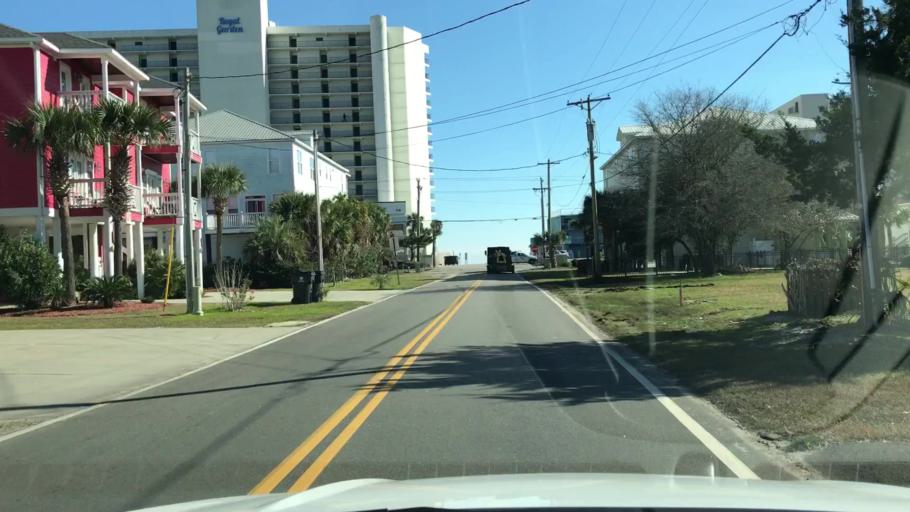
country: US
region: South Carolina
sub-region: Horry County
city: Garden City
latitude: 33.5862
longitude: -78.9918
